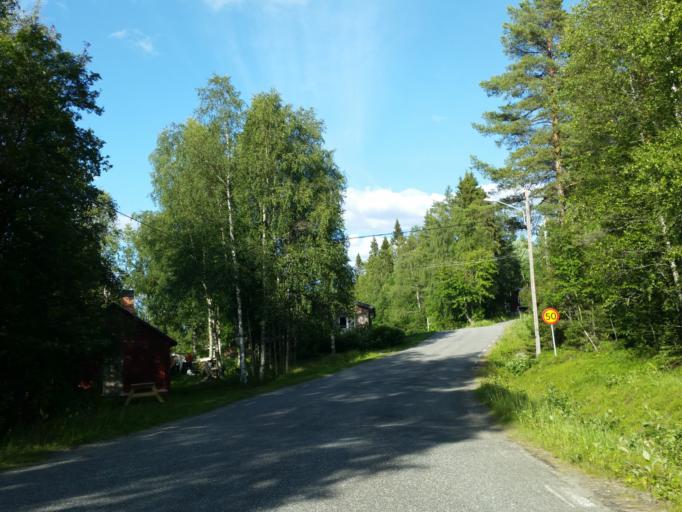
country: SE
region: Vaesterbotten
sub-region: Robertsfors Kommun
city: Robertsfors
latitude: 64.0371
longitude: 20.8517
